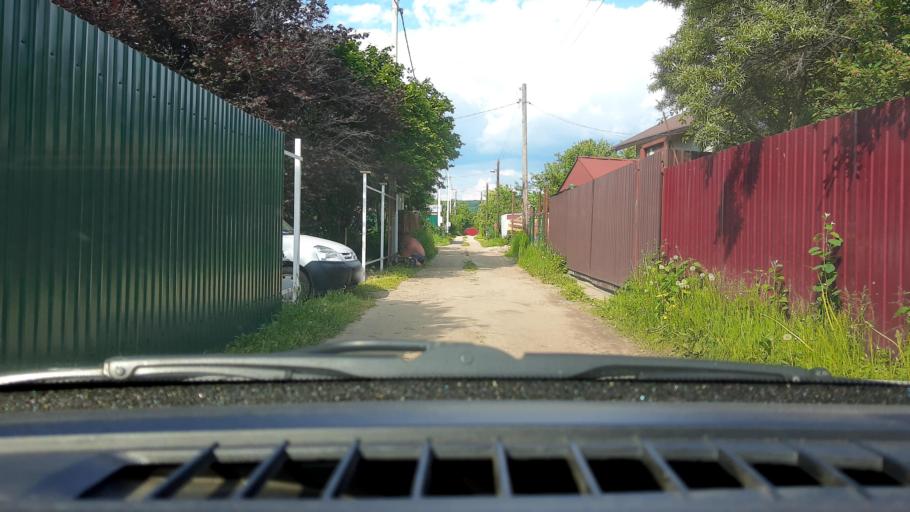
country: RU
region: Nizjnij Novgorod
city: Nizhniy Novgorod
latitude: 56.2574
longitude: 43.9442
